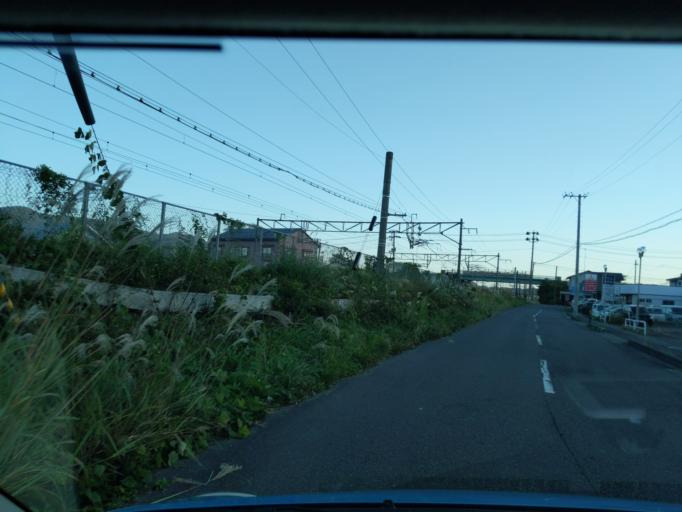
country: JP
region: Iwate
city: Mizusawa
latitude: 39.0479
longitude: 141.1261
